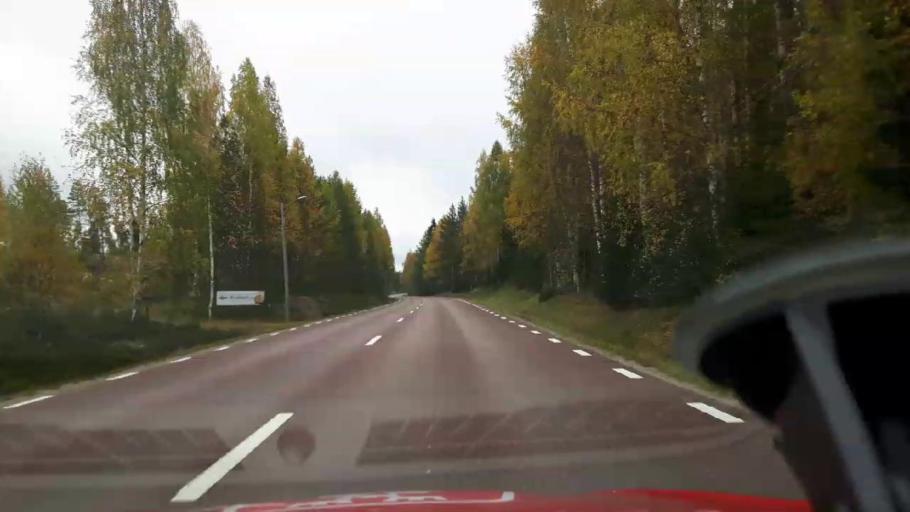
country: SE
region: Jaemtland
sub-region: Harjedalens Kommun
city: Sveg
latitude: 62.3112
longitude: 14.7577
